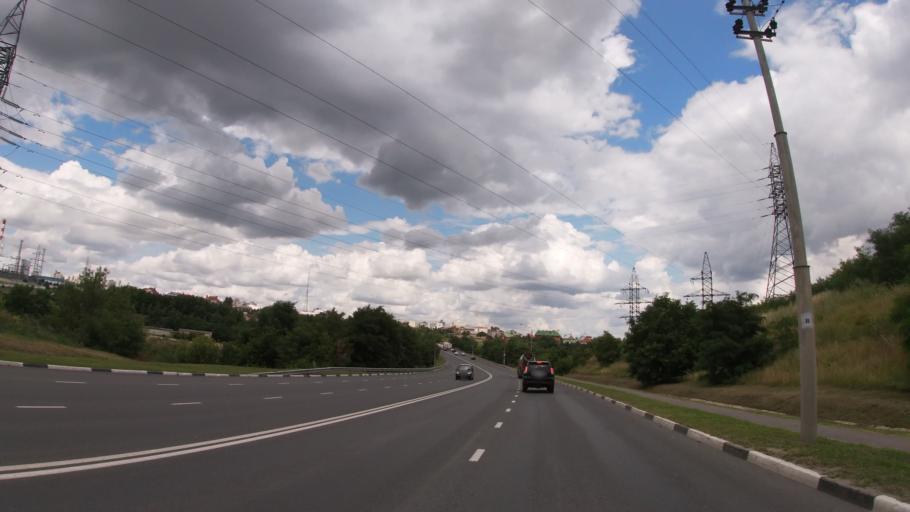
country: RU
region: Belgorod
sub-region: Belgorodskiy Rayon
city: Belgorod
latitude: 50.5576
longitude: 36.5859
